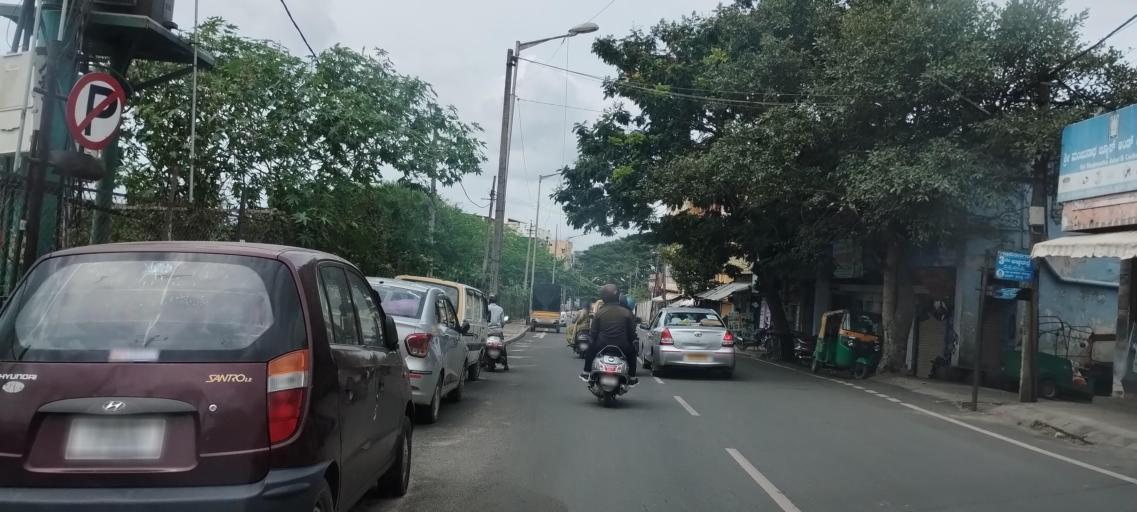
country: IN
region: Karnataka
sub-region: Bangalore Urban
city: Bangalore
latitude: 12.9474
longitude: 77.5386
